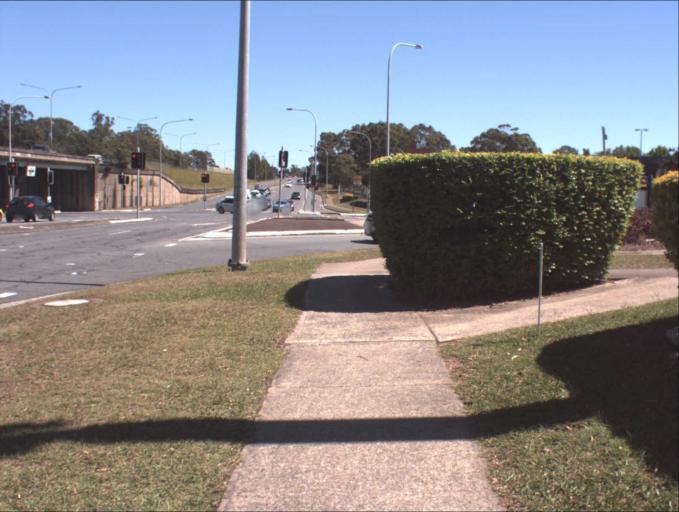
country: AU
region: Queensland
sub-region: Logan
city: Springwood
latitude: -27.6107
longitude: 153.1226
